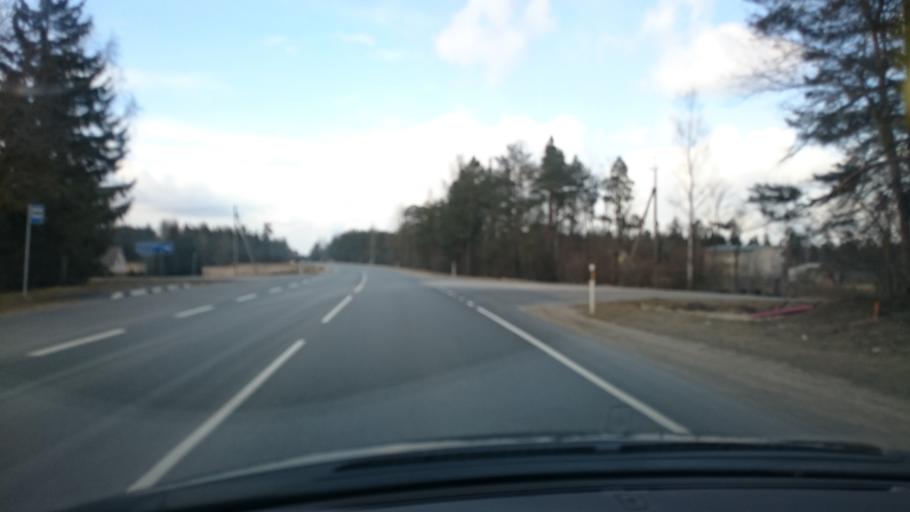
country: EE
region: Harju
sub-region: Nissi vald
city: Turba
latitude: 59.0999
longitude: 24.2523
